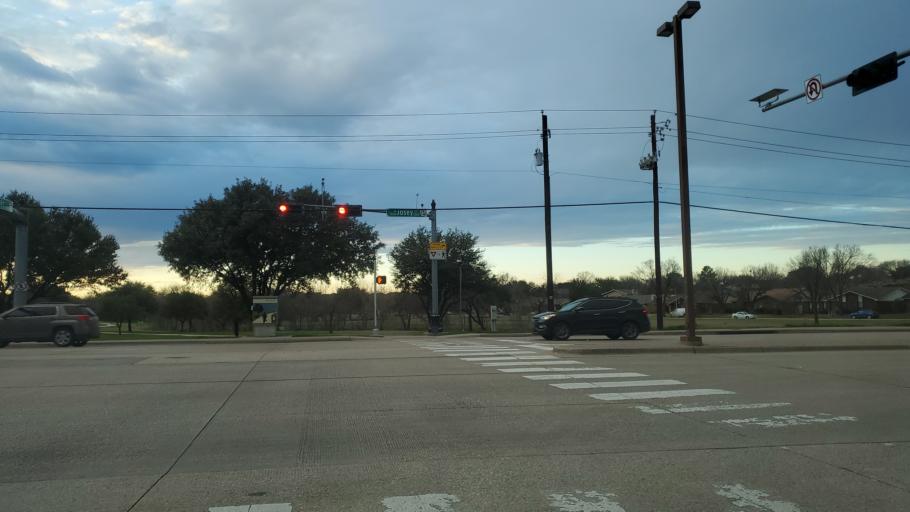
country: US
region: Texas
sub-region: Dallas County
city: Carrollton
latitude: 32.9957
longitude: -96.8865
